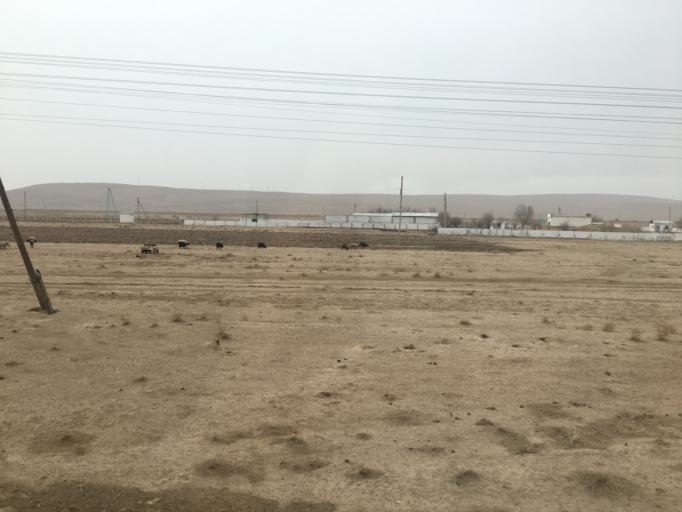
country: TM
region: Mary
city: Serhetabat
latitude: 35.6098
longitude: 62.5390
